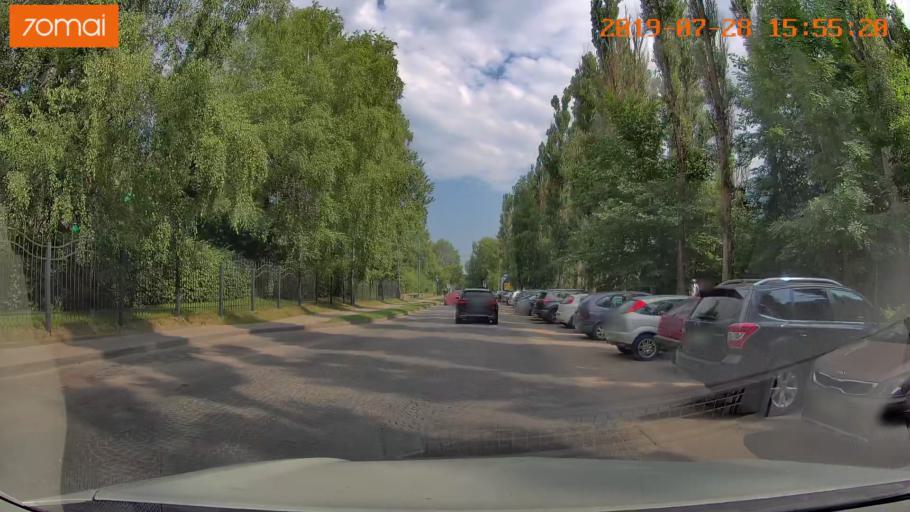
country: RU
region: Kaliningrad
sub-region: Gorod Svetlogorsk
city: Svetlogorsk
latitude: 54.9411
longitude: 20.1390
